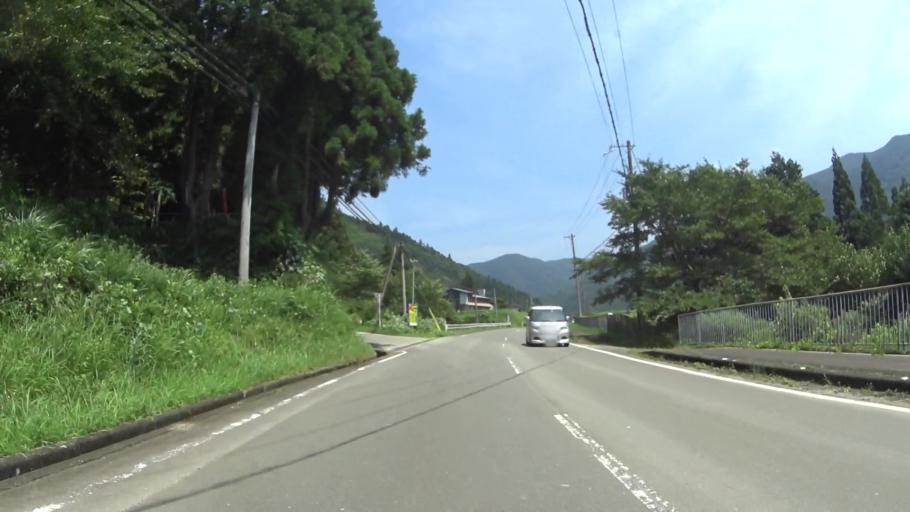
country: JP
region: Kyoto
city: Ayabe
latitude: 35.2684
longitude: 135.4302
